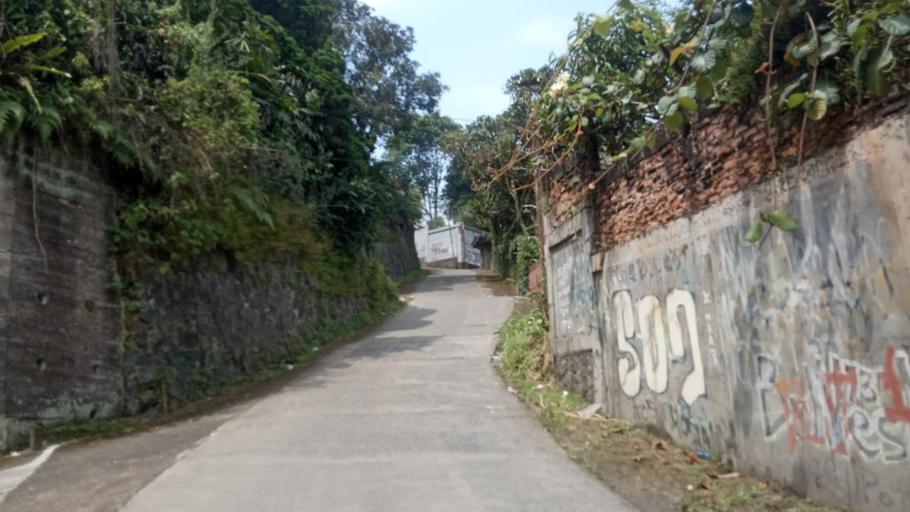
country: ID
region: West Java
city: Caringin
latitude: -6.6493
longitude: 106.8871
